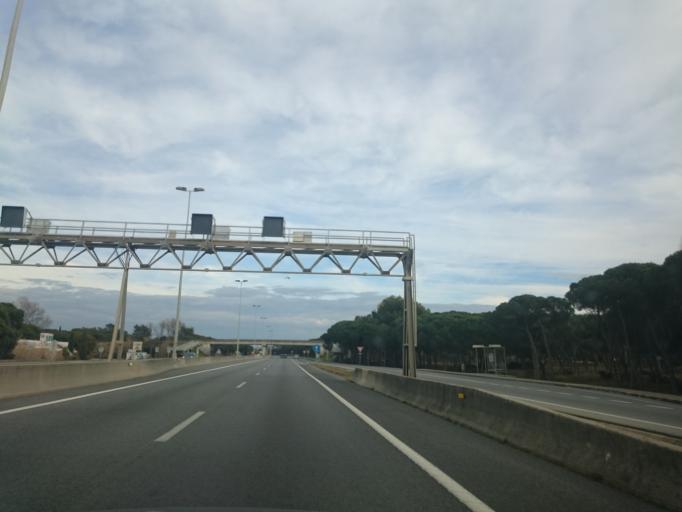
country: ES
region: Catalonia
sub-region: Provincia de Barcelona
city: Viladecans
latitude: 41.2717
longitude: 2.0354
